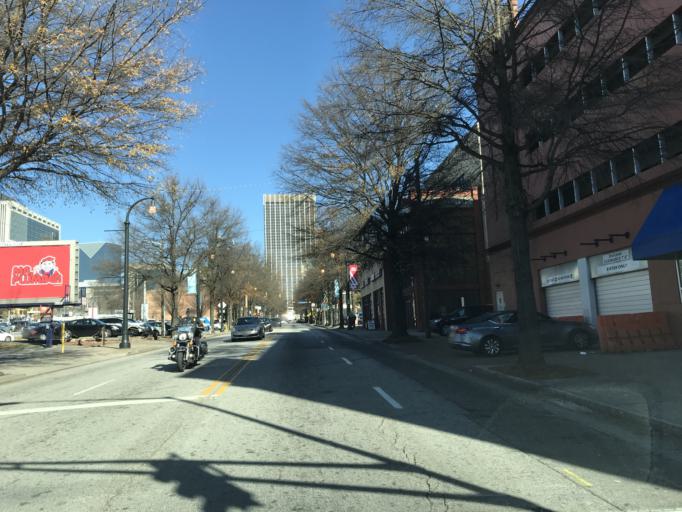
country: US
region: Georgia
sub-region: Fulton County
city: Atlanta
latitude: 33.7488
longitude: -84.3947
